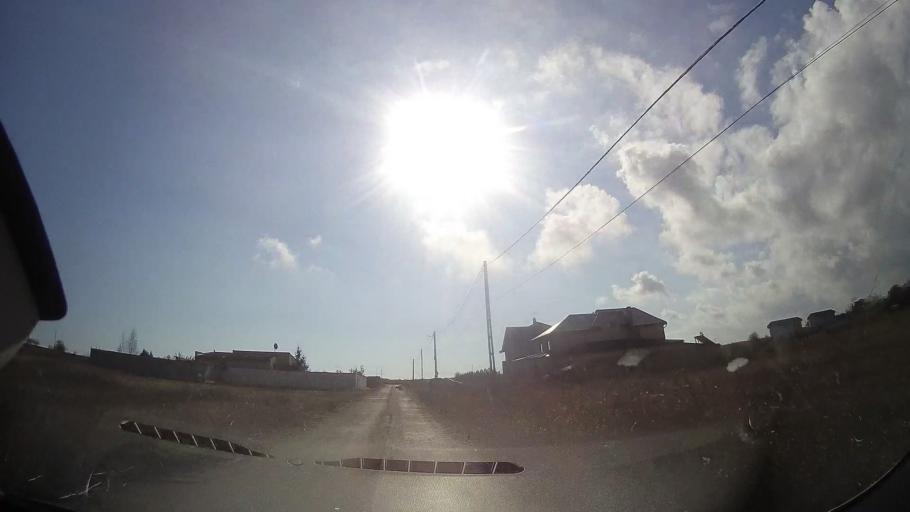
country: RO
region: Constanta
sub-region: Comuna Tuzla
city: Tuzla
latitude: 43.9967
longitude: 28.6443
